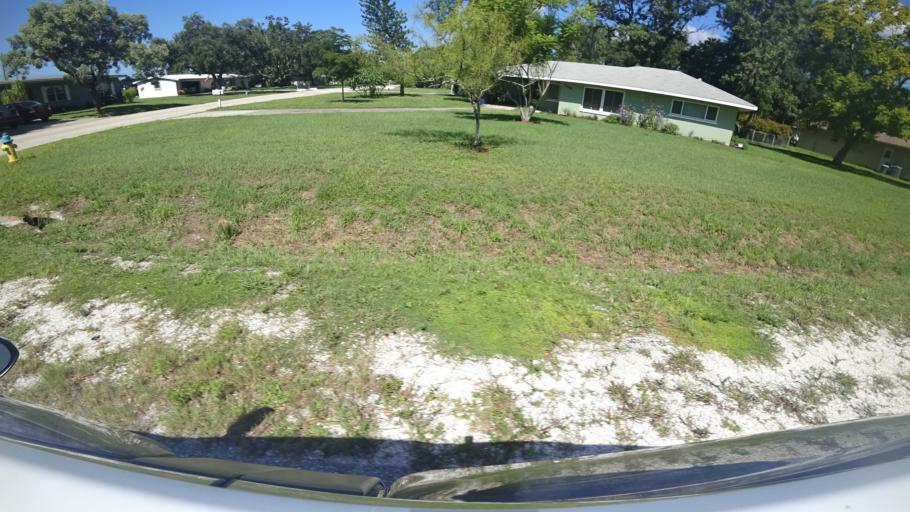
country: US
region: Florida
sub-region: Manatee County
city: South Bradenton
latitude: 27.4494
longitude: -82.5918
